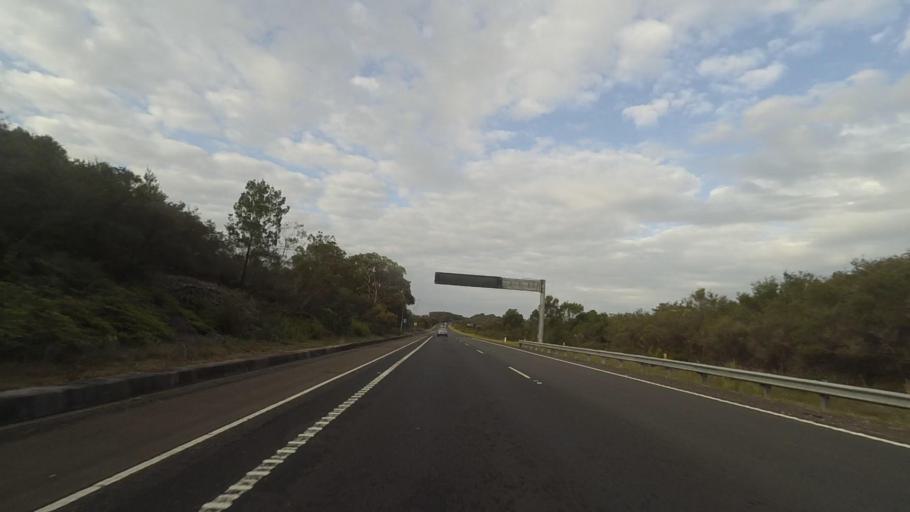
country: AU
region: New South Wales
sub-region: Wollongong
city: Bulli
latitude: -34.2536
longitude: 150.9331
